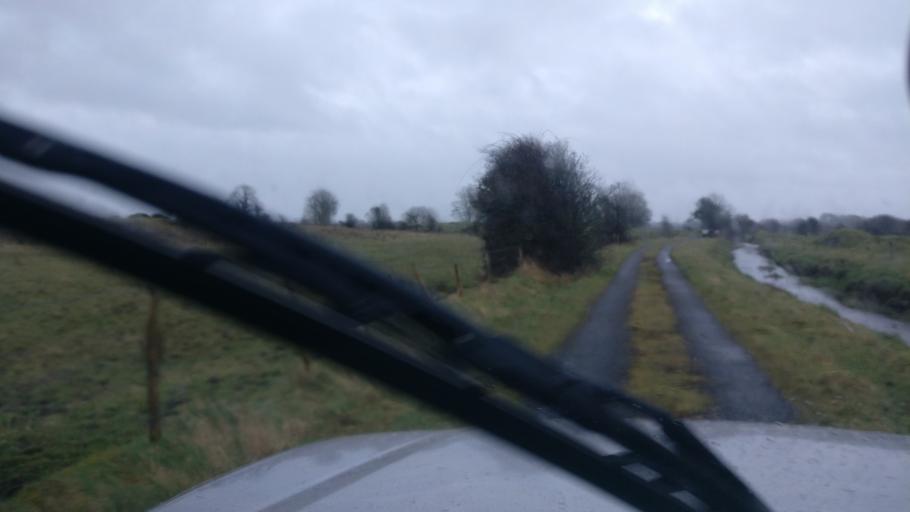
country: IE
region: Connaught
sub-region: County Galway
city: Ballinasloe
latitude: 53.2431
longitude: -8.3364
